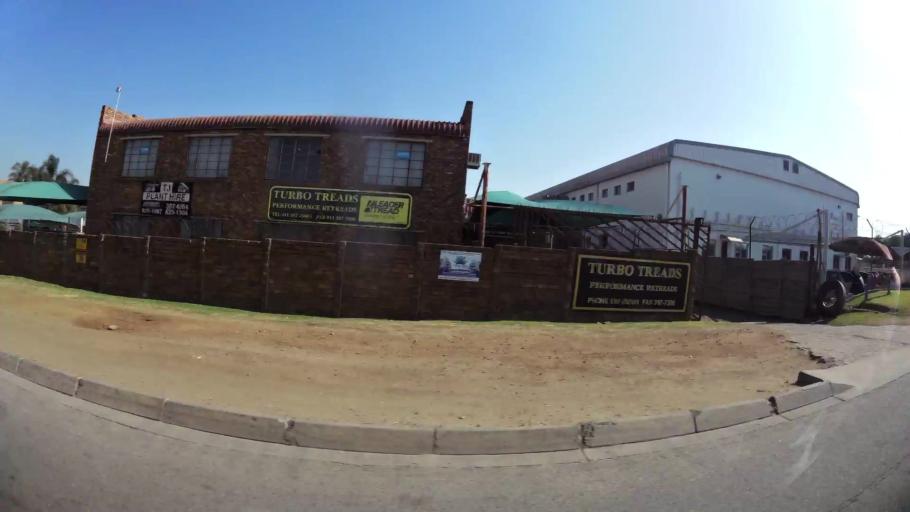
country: ZA
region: Gauteng
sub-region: Ekurhuleni Metropolitan Municipality
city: Boksburg
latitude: -26.1665
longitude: 28.2335
